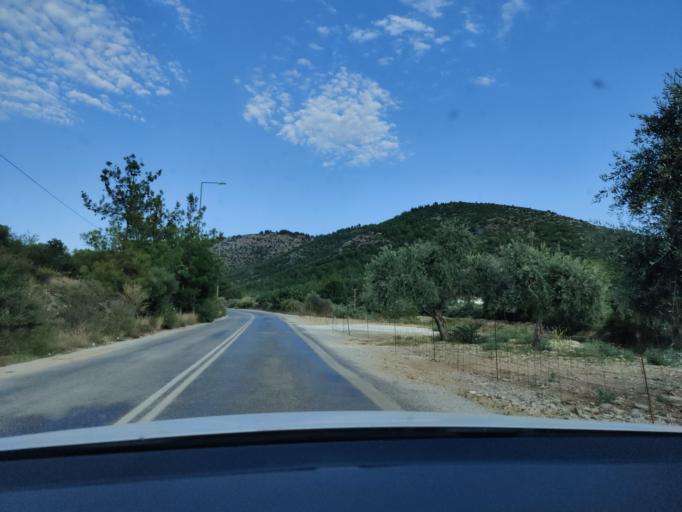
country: GR
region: East Macedonia and Thrace
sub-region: Nomos Kavalas
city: Limenaria
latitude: 40.6133
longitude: 24.6266
